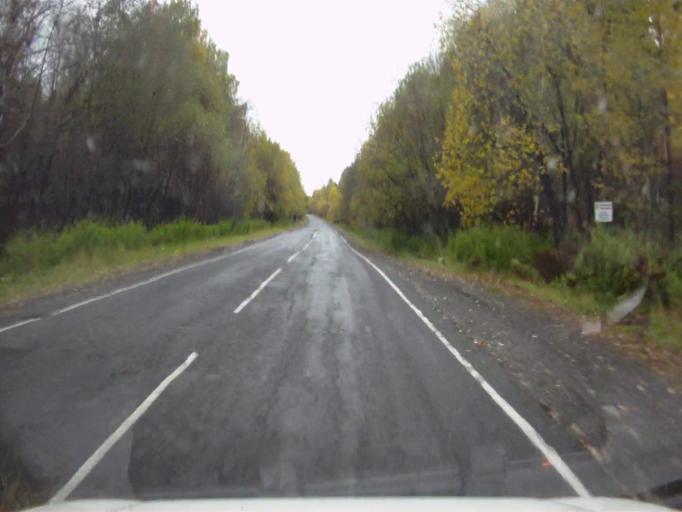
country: RU
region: Chelyabinsk
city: Verkhniy Ufaley
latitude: 56.0466
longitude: 60.1164
